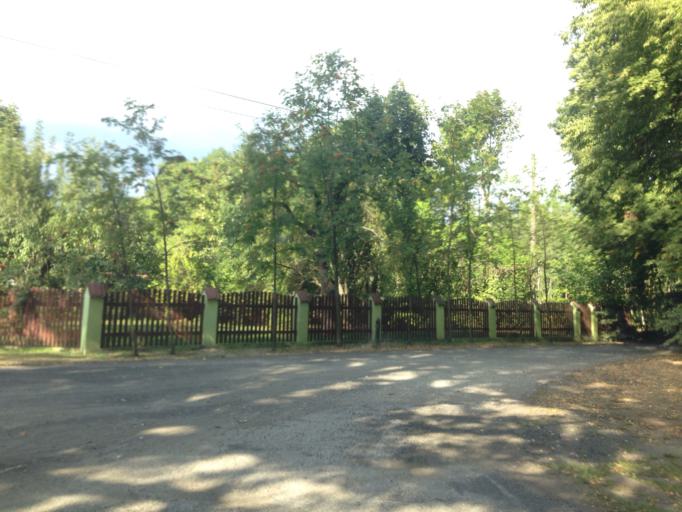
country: PL
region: Kujawsko-Pomorskie
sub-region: Powiat swiecki
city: Swiekatowo
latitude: 53.4852
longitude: 18.1273
